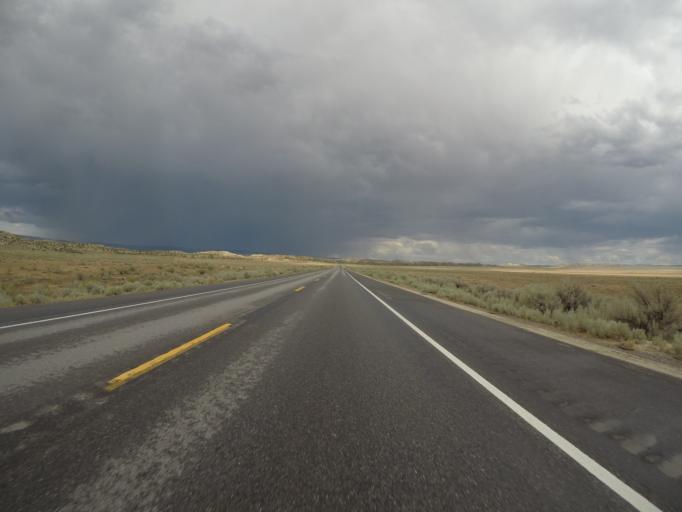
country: US
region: Colorado
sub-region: Rio Blanco County
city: Rangely
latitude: 40.2824
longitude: -109.0926
